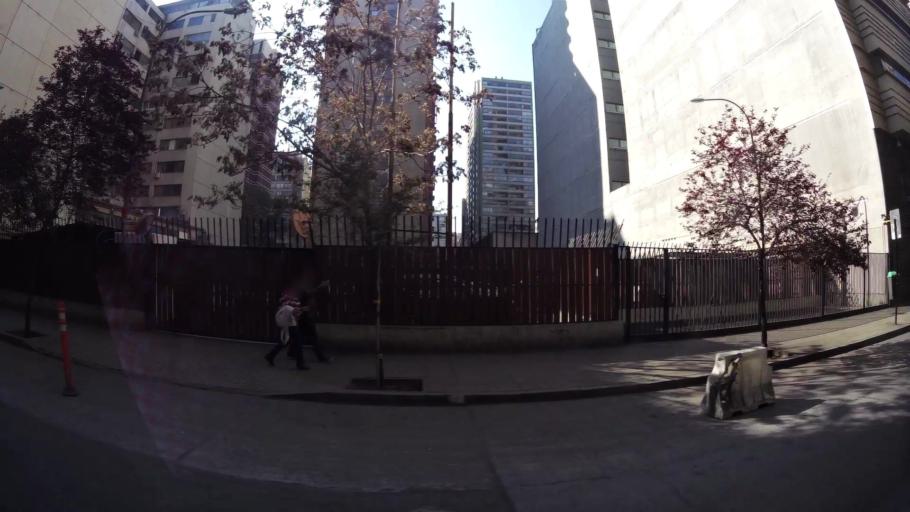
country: CL
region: Santiago Metropolitan
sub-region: Provincia de Santiago
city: Santiago
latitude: -33.4379
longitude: -70.6561
